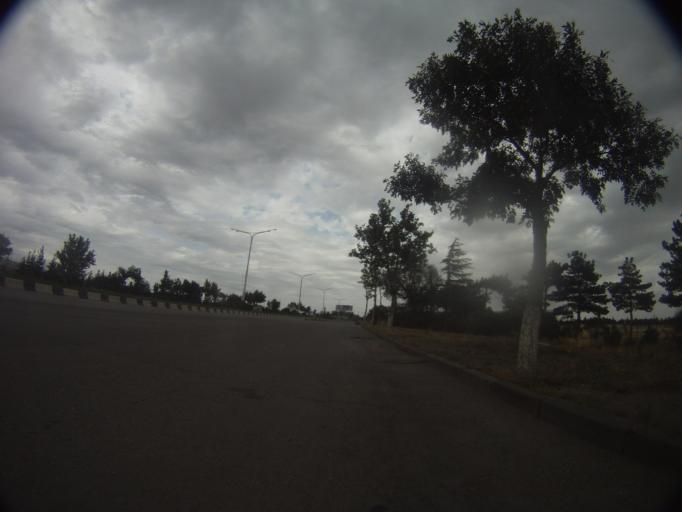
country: GE
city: Didi Lilo
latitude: 41.6887
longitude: 45.0160
